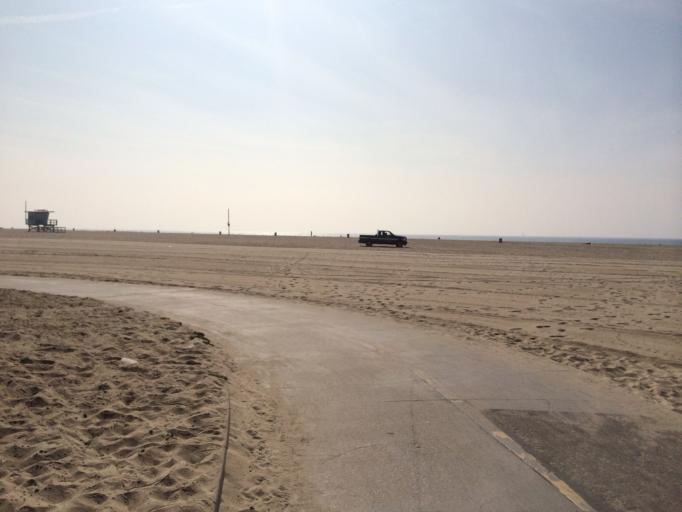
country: US
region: California
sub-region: Los Angeles County
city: Santa Monica
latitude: 33.9940
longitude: -118.4809
